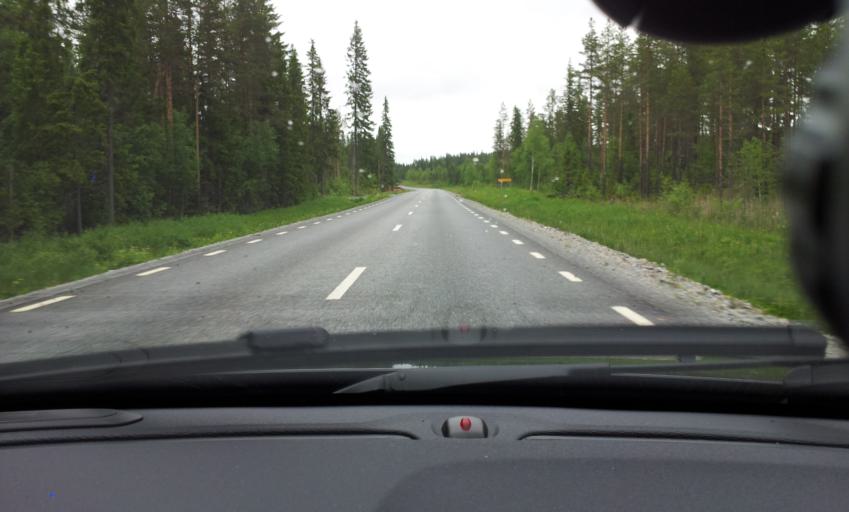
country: SE
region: Jaemtland
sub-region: OEstersunds Kommun
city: Lit
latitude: 63.7051
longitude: 14.6903
